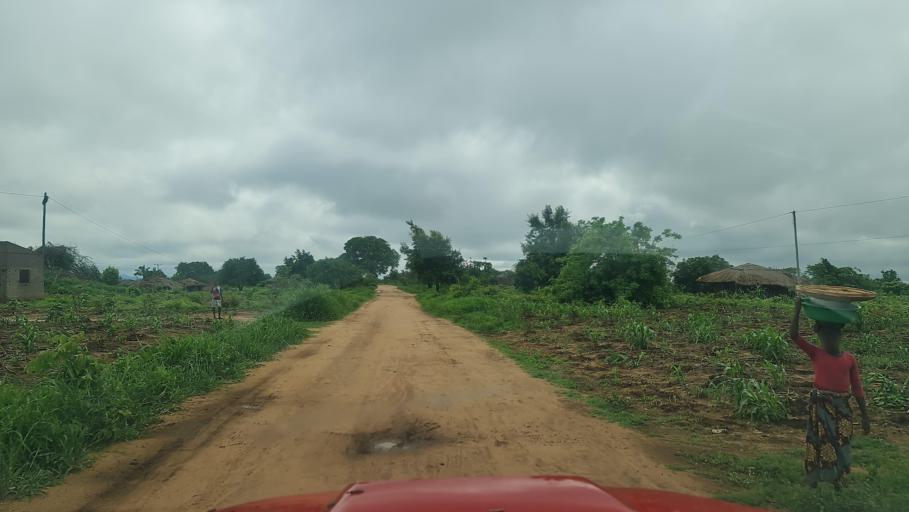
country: MW
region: Southern Region
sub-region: Nsanje District
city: Nsanje
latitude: -17.1899
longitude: 35.7110
